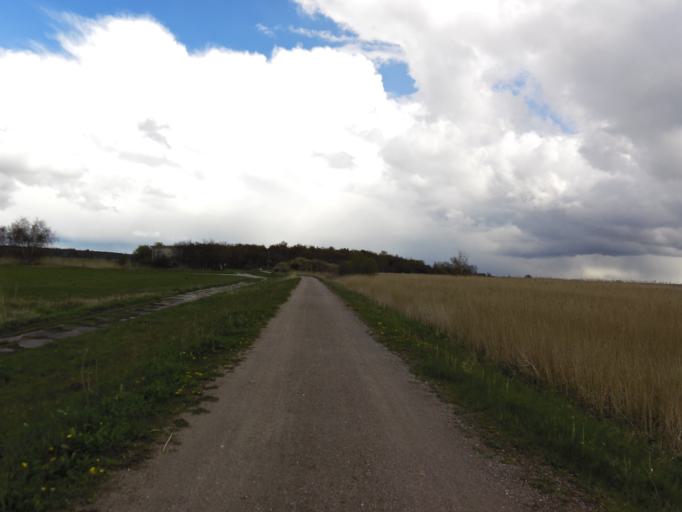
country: DE
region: Mecklenburg-Vorpommern
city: Born
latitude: 54.3827
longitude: 12.4931
